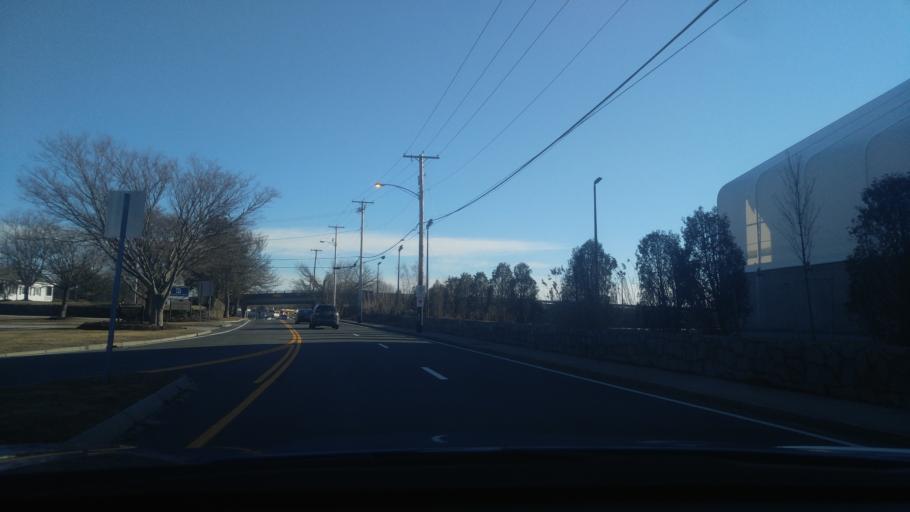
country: US
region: Rhode Island
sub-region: Washington County
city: Wakefield-Peacedale
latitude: 41.4336
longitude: -71.4827
